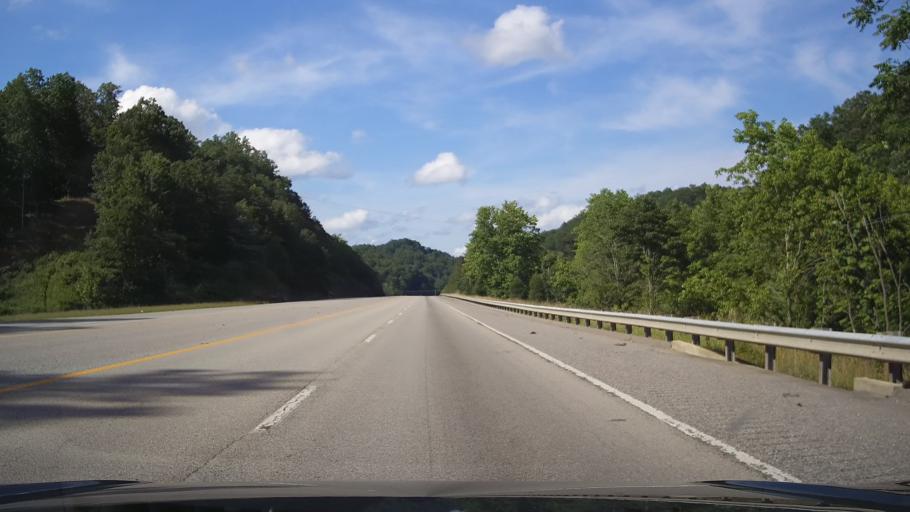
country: US
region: Kentucky
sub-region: Lawrence County
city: Louisa
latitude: 38.0423
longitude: -82.6474
